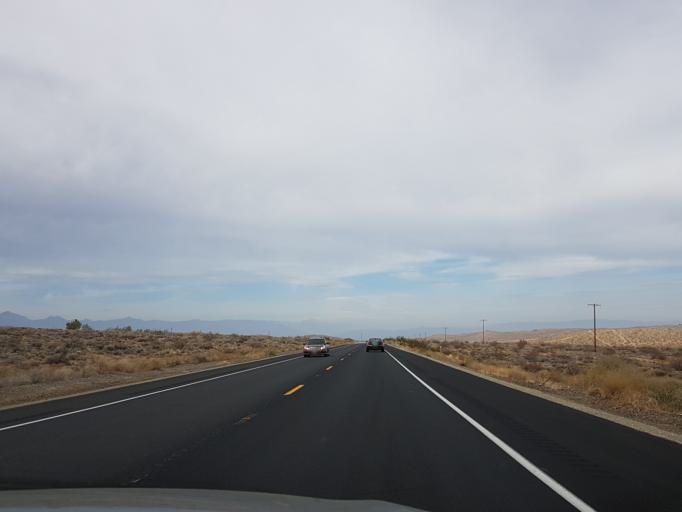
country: US
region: California
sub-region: Kern County
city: Ridgecrest
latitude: 35.4920
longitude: -117.6602
